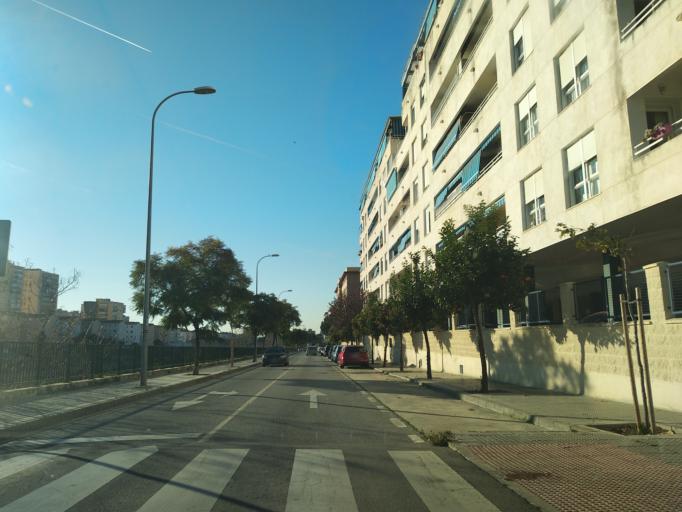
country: ES
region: Andalusia
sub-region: Provincia de Malaga
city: Malaga
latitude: 36.7474
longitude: -4.4251
